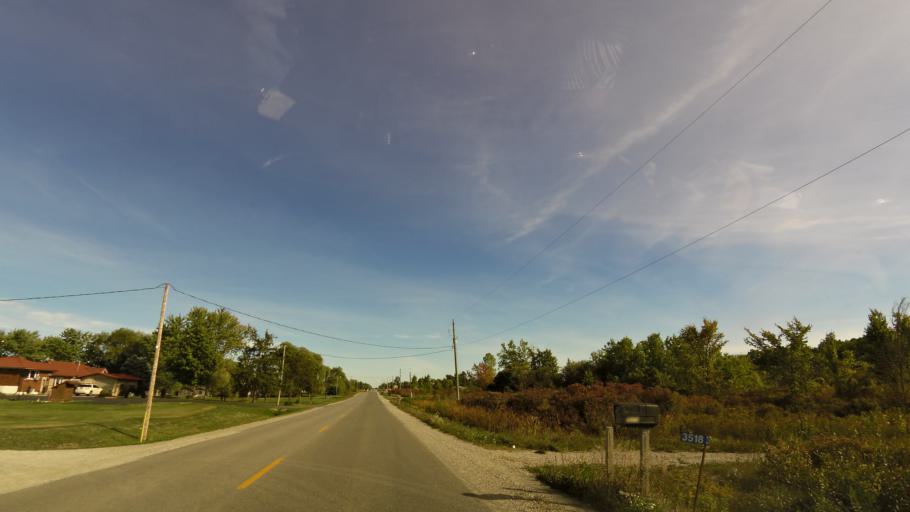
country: CA
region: Ontario
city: Ancaster
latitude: 43.0342
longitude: -80.0243
